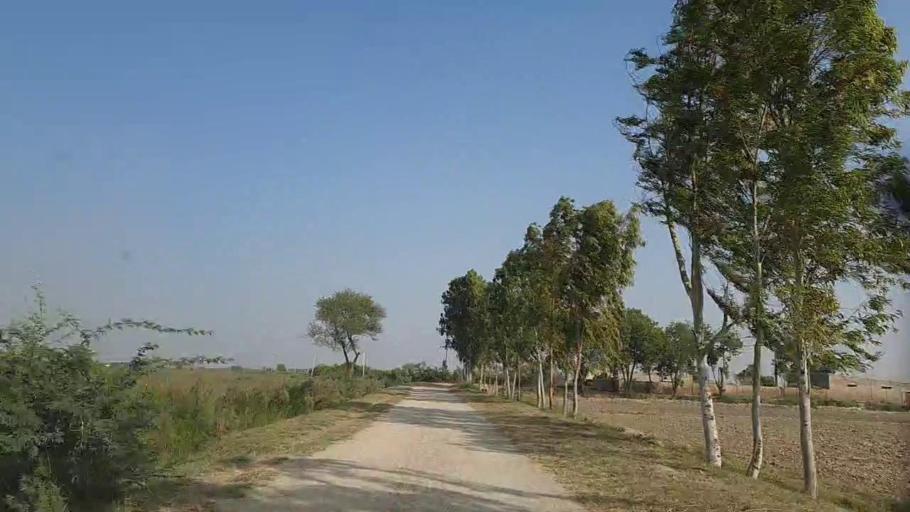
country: PK
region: Sindh
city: Mirpur Batoro
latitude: 24.5791
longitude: 68.2240
